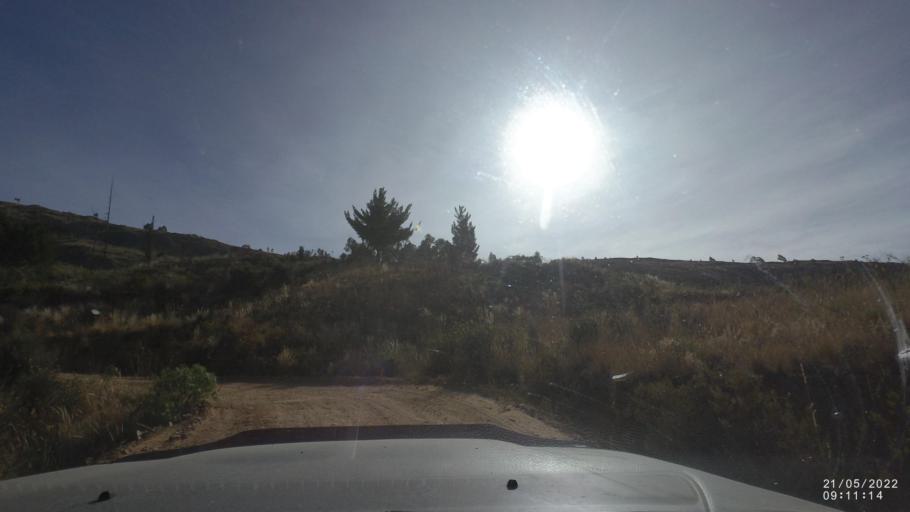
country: BO
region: Cochabamba
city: Cochabamba
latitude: -17.3715
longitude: -66.0229
